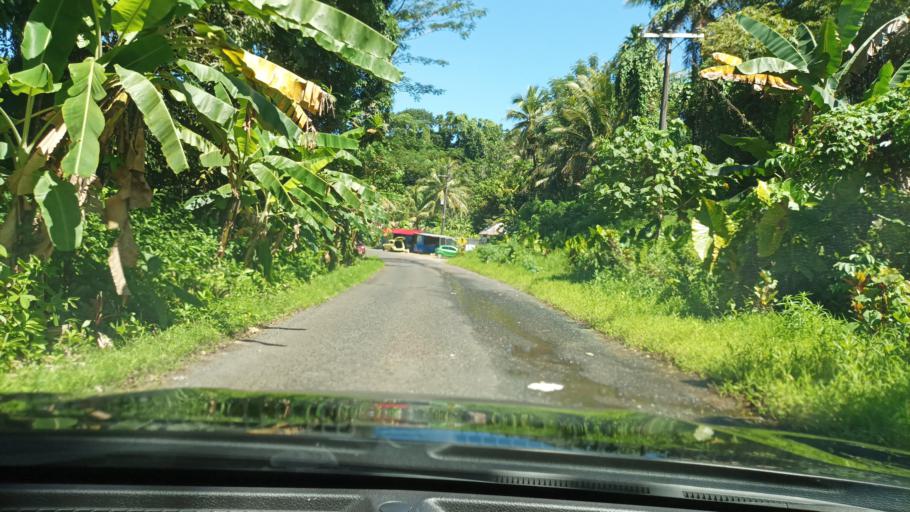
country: FM
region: Pohnpei
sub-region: Madolenihm Municipality
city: Madolenihm Municipality Government
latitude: 6.8472
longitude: 158.3013
